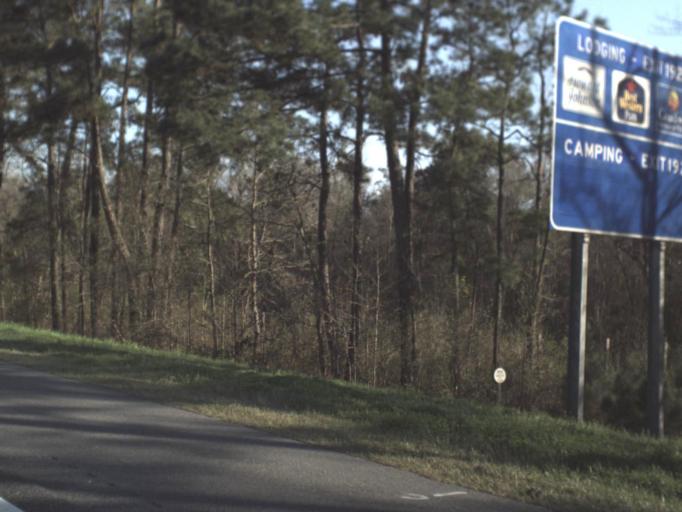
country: US
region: Florida
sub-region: Gadsden County
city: Midway
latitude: 30.4950
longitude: -84.4453
